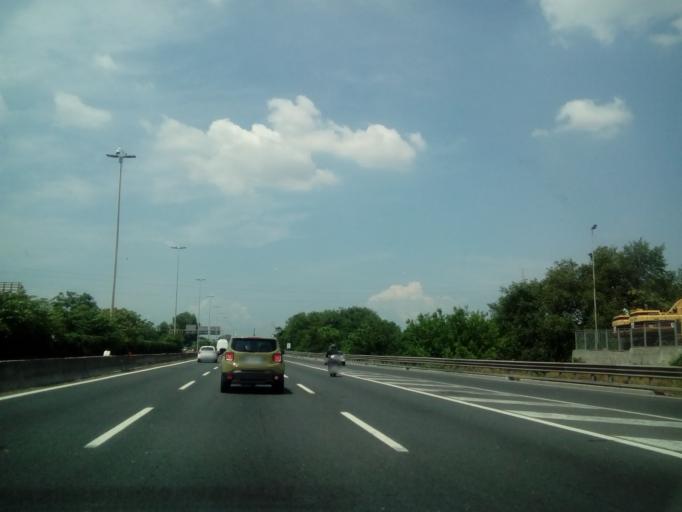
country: IT
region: Latium
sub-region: Citta metropolitana di Roma Capitale
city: Setteville
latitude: 41.8961
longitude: 12.6154
